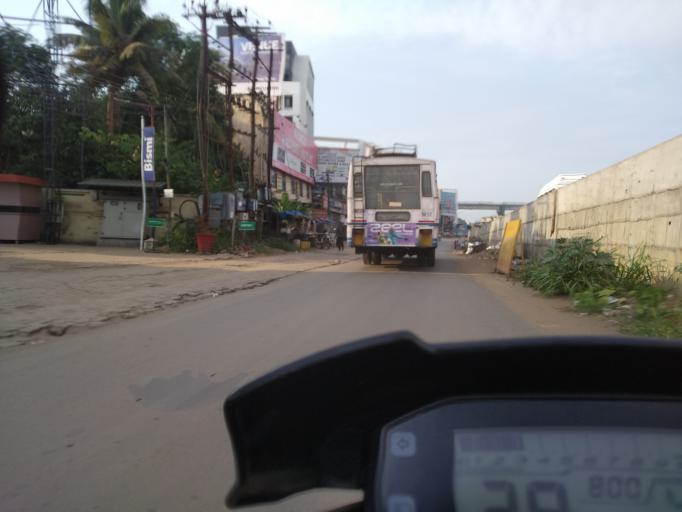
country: IN
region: Kerala
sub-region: Ernakulam
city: Cochin
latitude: 9.9712
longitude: 76.3183
